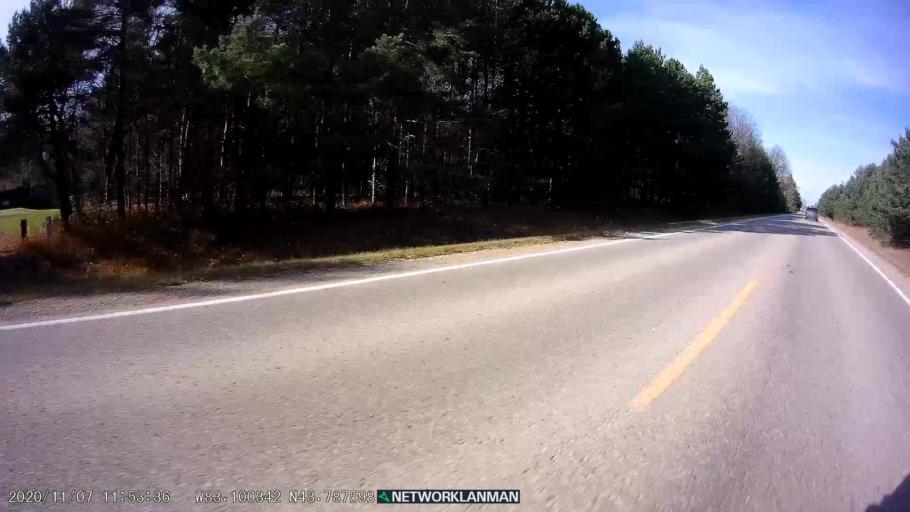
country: US
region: Michigan
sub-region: Huron County
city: Bad Axe
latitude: 43.7879
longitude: -83.1004
